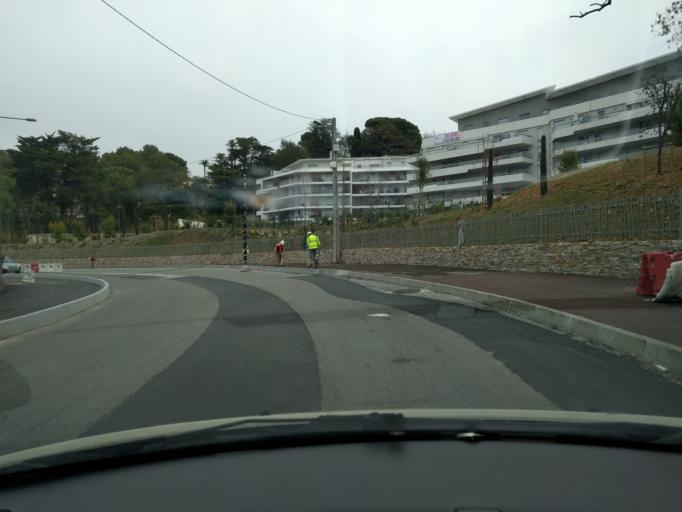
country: FR
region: Provence-Alpes-Cote d'Azur
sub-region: Departement des Alpes-Maritimes
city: La Roquette-sur-Siagne
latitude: 43.5708
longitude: 6.9551
